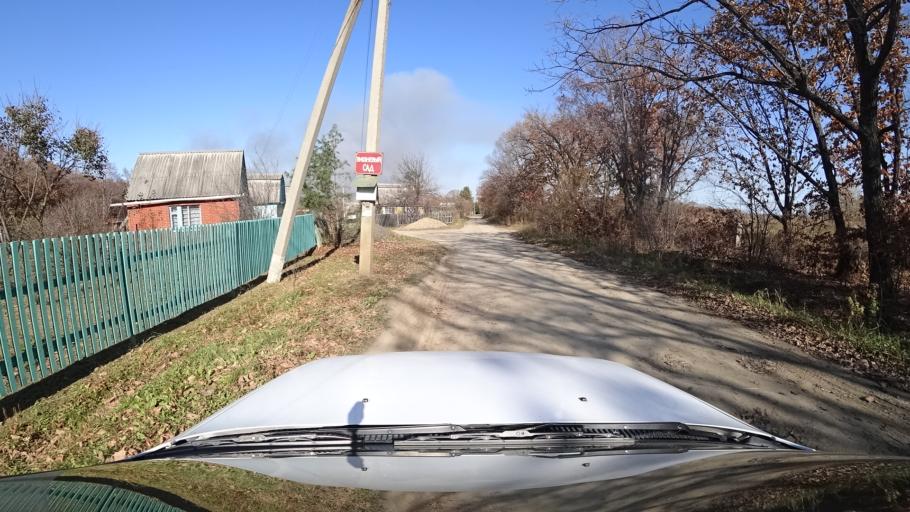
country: RU
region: Primorskiy
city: Dal'nerechensk
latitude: 45.8842
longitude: 133.7400
